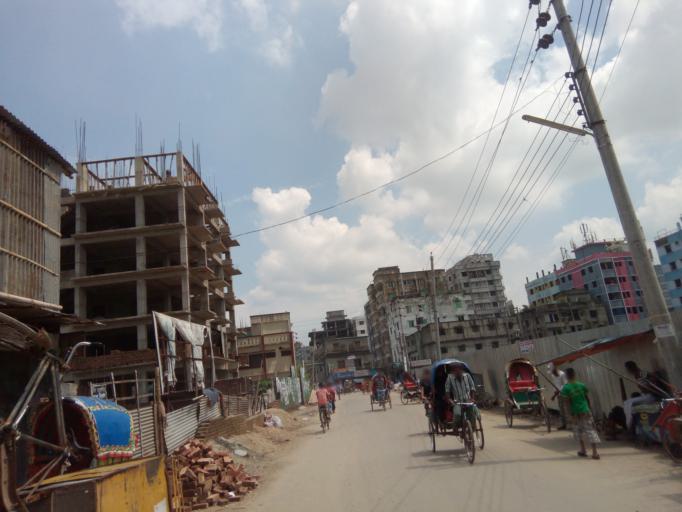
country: BD
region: Dhaka
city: Azimpur
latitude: 23.7461
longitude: 90.3624
